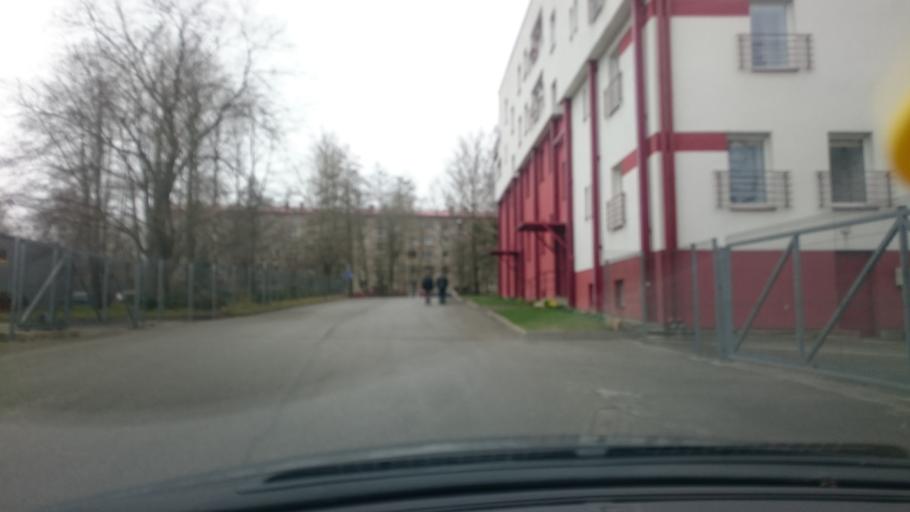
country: EE
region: Harju
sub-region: Tallinna linn
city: Tallinn
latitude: 59.4572
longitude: 24.6885
